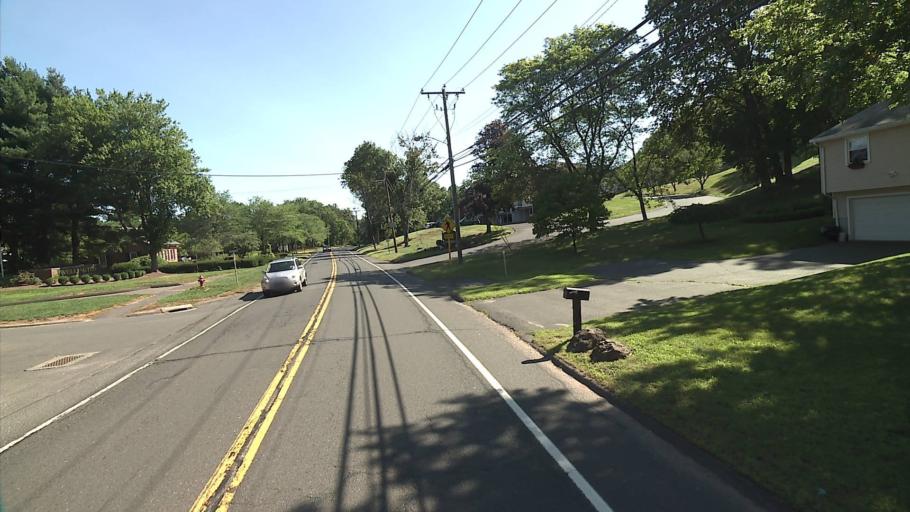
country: US
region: Connecticut
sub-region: Hartford County
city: Farmington
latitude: 41.7107
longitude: -72.8399
